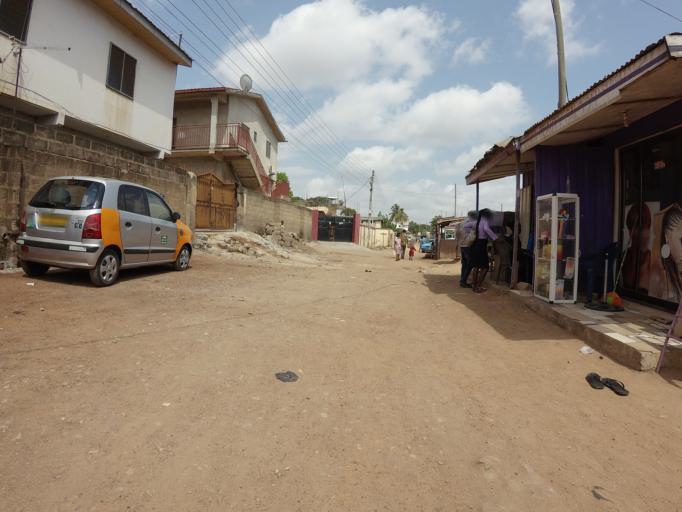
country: GH
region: Greater Accra
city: Dome
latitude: 5.6188
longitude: -0.2486
